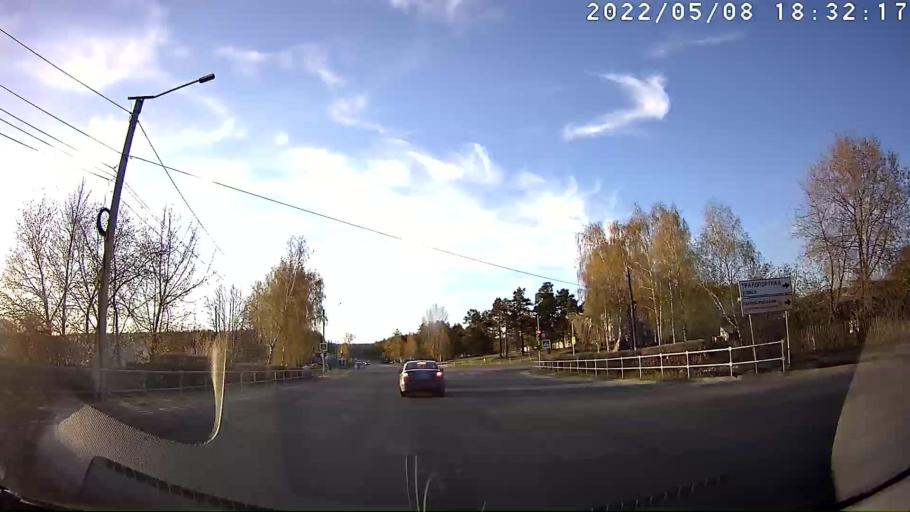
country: RU
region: Mariy-El
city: Volzhsk
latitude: 55.8864
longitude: 48.3597
